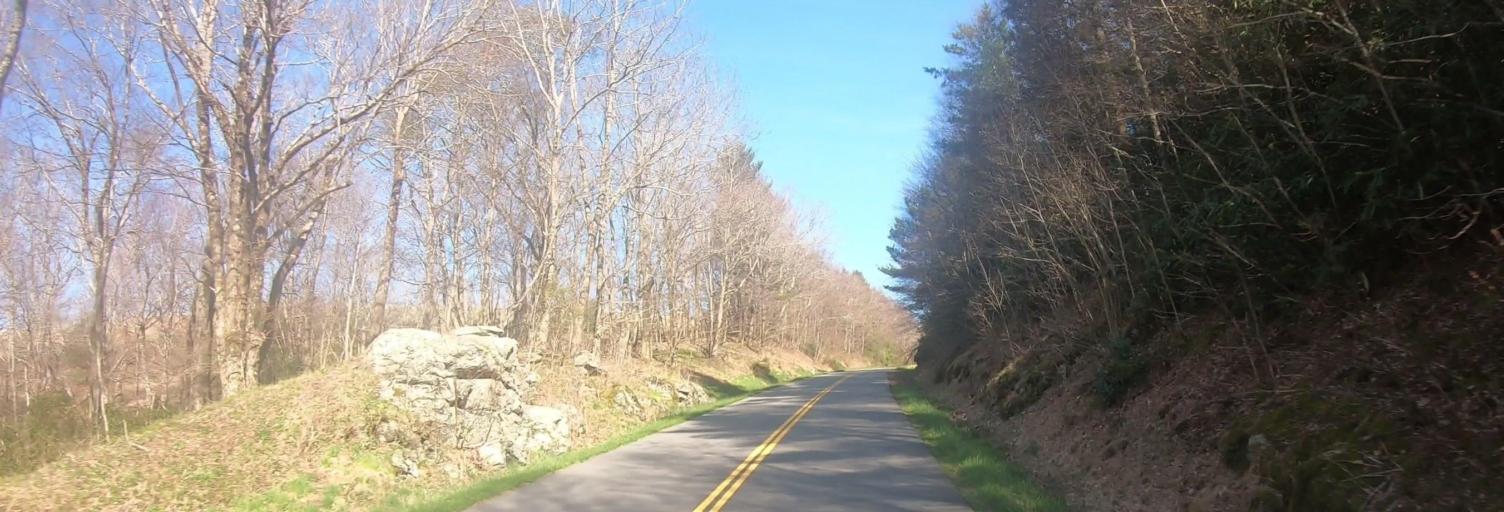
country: US
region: North Carolina
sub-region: Watauga County
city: Blowing Rock
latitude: 36.1396
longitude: -81.6535
